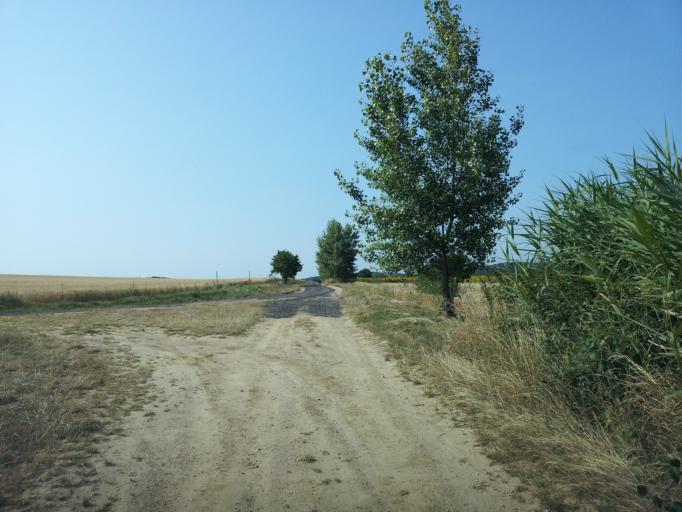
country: HU
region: Zala
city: Cserszegtomaj
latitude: 46.8464
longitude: 17.2311
